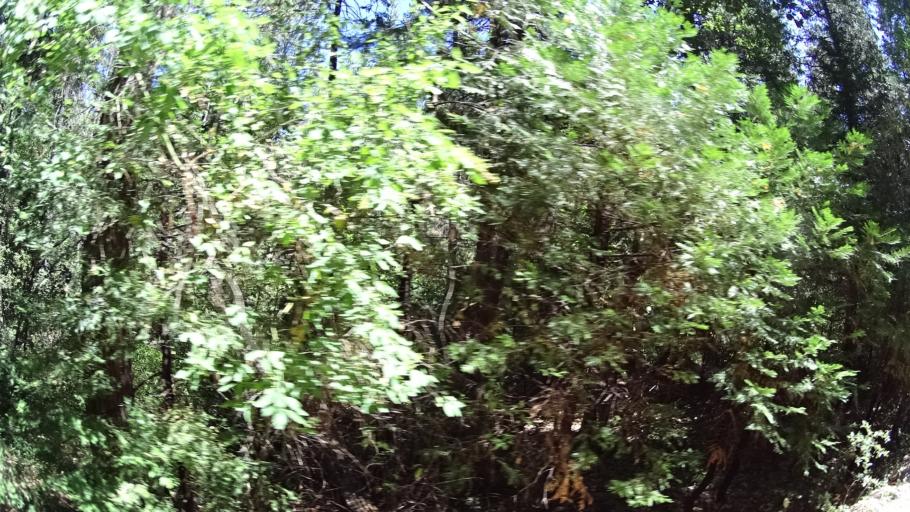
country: US
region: California
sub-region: Amador County
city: Pioneer
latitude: 38.3547
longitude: -120.5553
